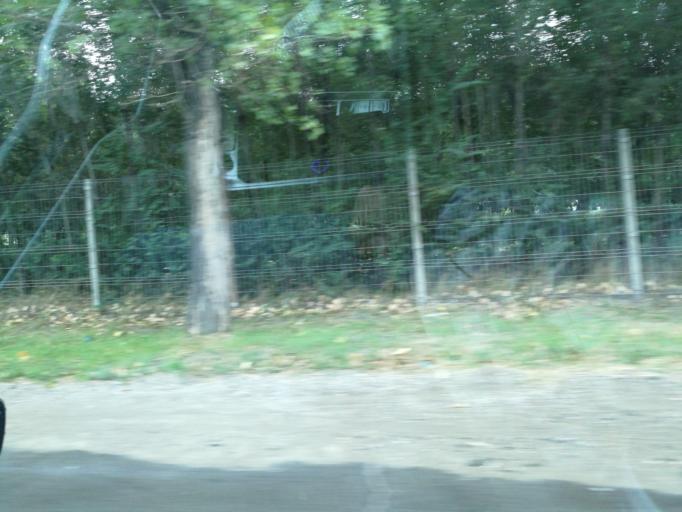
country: RO
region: Galati
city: Galati
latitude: 45.4476
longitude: 28.0120
